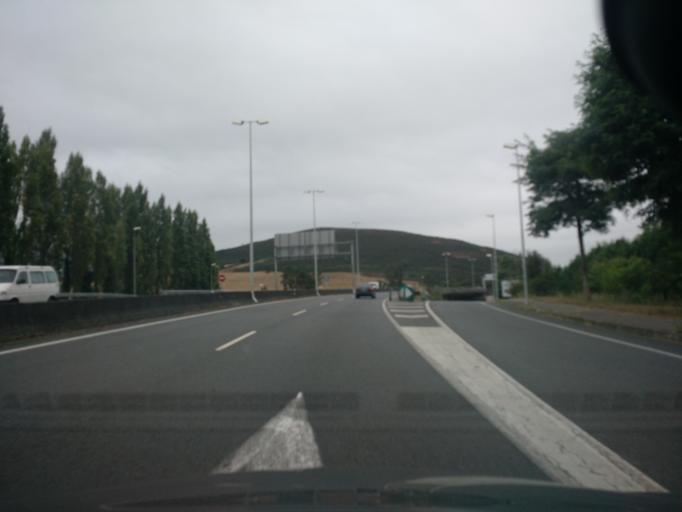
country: ES
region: Galicia
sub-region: Provincia da Coruna
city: Santiago de Compostela
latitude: 42.8838
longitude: -8.5112
